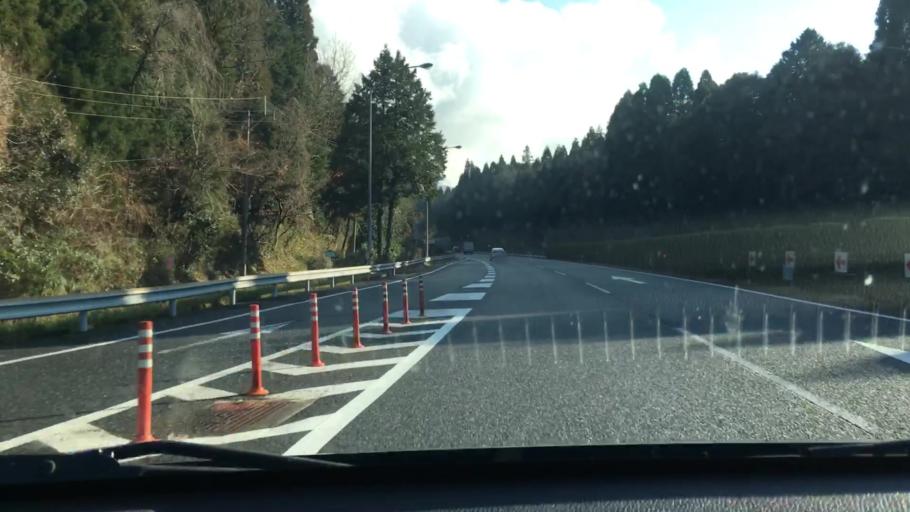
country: JP
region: Kagoshima
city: Okuchi-shinohara
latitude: 32.0047
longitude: 130.7559
